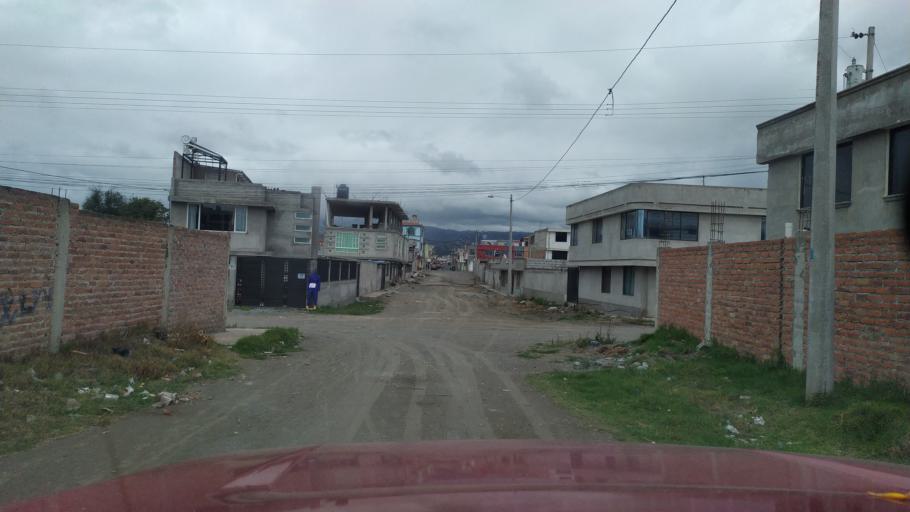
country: EC
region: Chimborazo
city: Riobamba
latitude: -1.6589
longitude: -78.6366
